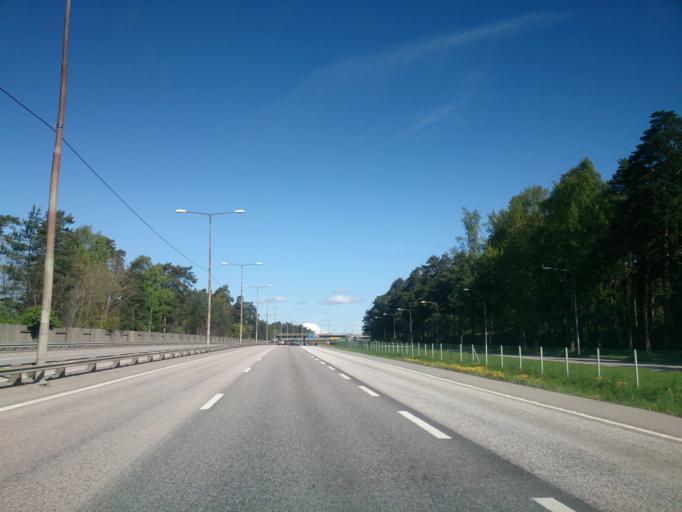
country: SE
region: Stockholm
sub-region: Stockholms Kommun
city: Arsta
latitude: 59.2694
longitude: 18.0956
